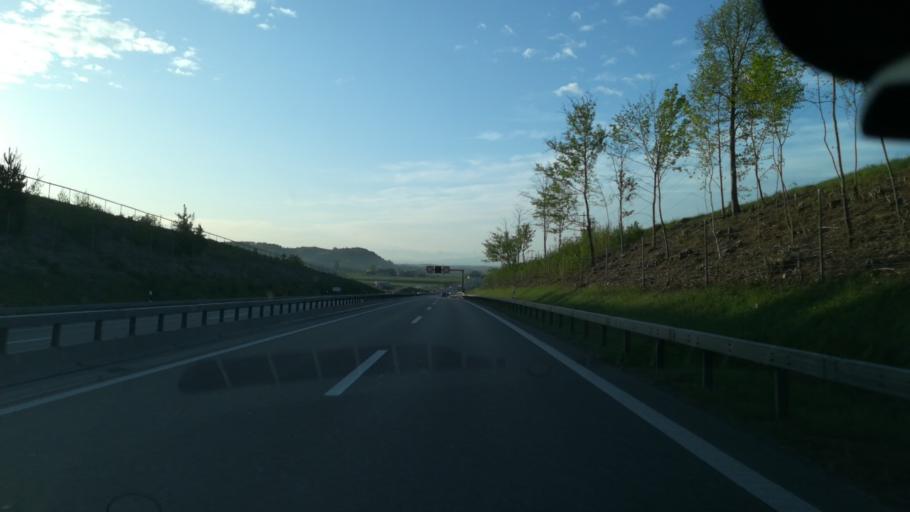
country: CH
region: Zurich
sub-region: Bezirk Andelfingen
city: Uhwiesen
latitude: 47.6588
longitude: 8.6314
